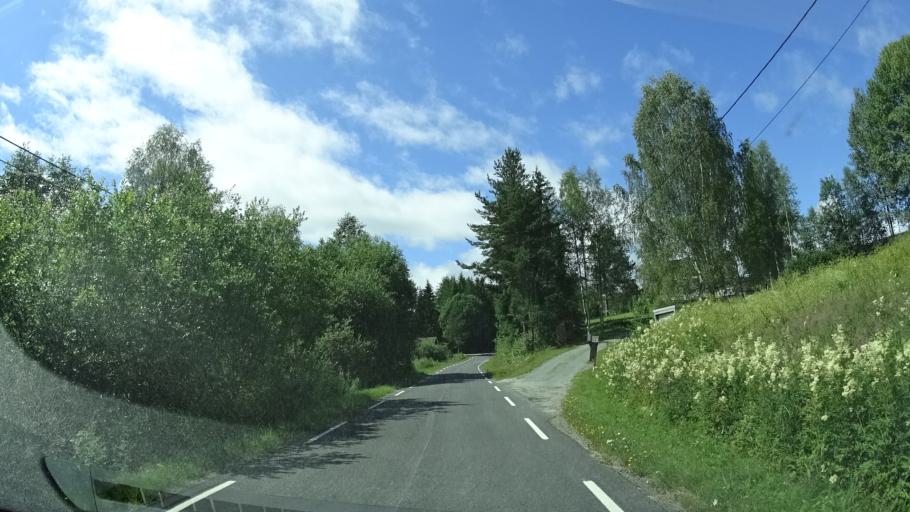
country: NO
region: Buskerud
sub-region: Krodsherad
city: Noresund
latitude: 60.2409
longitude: 9.8667
